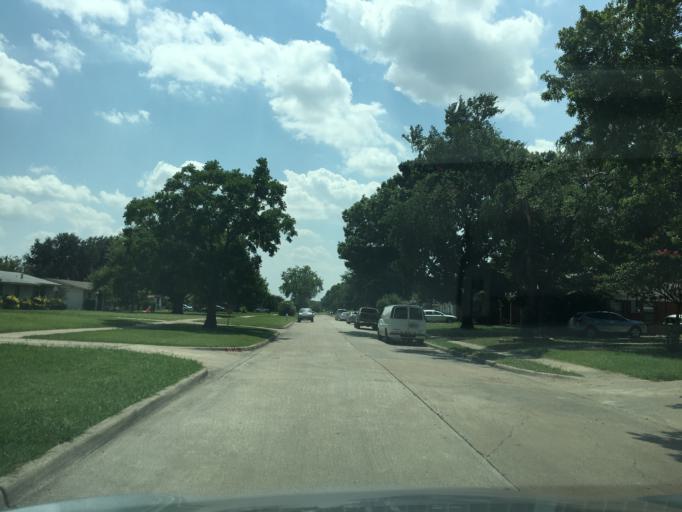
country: US
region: Texas
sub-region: Dallas County
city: Farmers Branch
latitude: 32.9175
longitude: -96.8601
